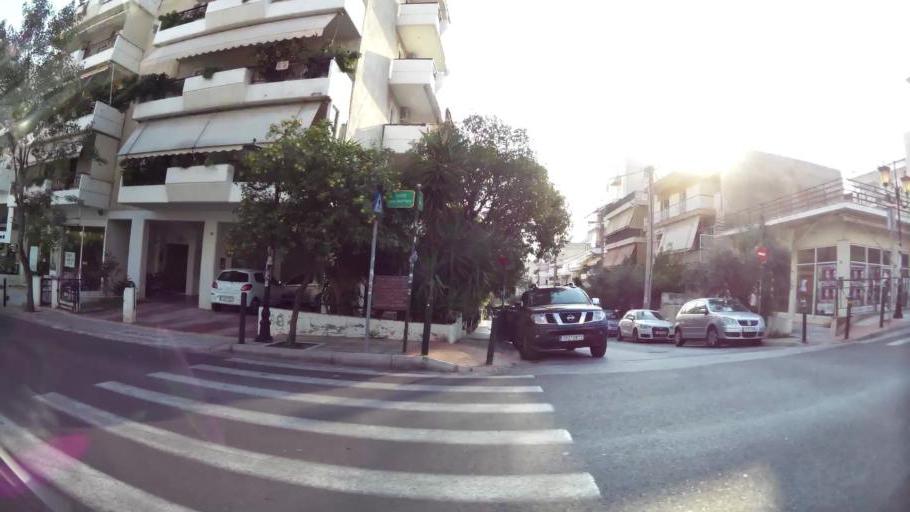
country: GR
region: Attica
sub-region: Nomarchia Athinas
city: Petroupolis
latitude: 38.0449
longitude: 23.6785
